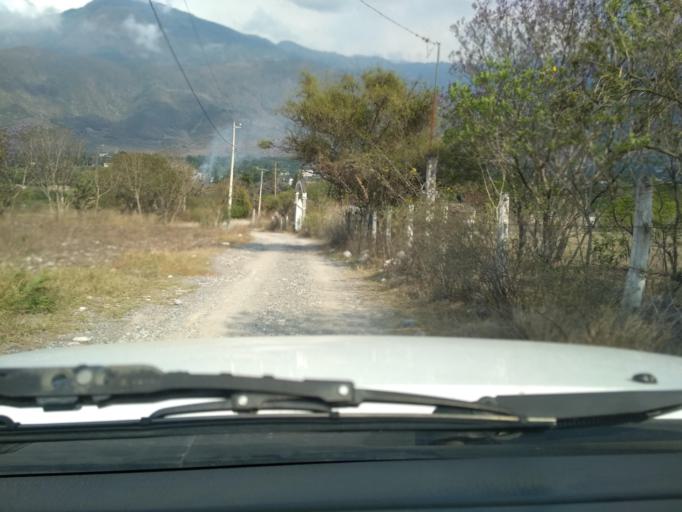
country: MX
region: Veracruz
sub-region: Acultzingo
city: Sierra de Agua
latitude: 18.7690
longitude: -97.2305
